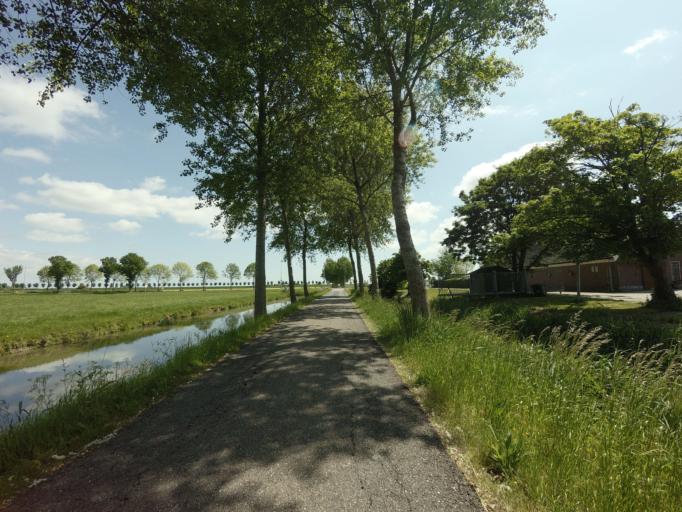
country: NL
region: North Holland
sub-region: Gemeente Beemster
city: Halfweg
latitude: 52.5959
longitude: 4.9401
